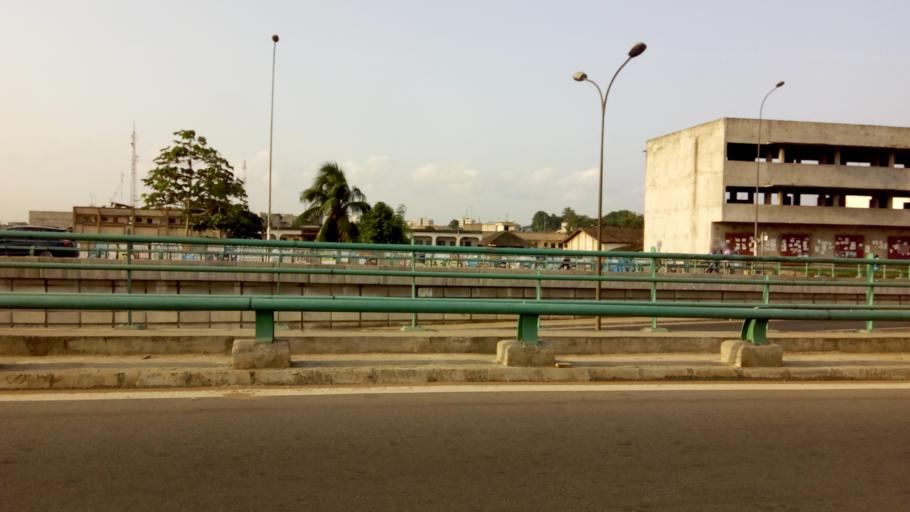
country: CI
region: Lagunes
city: Abidjan
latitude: 5.3536
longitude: -3.9781
